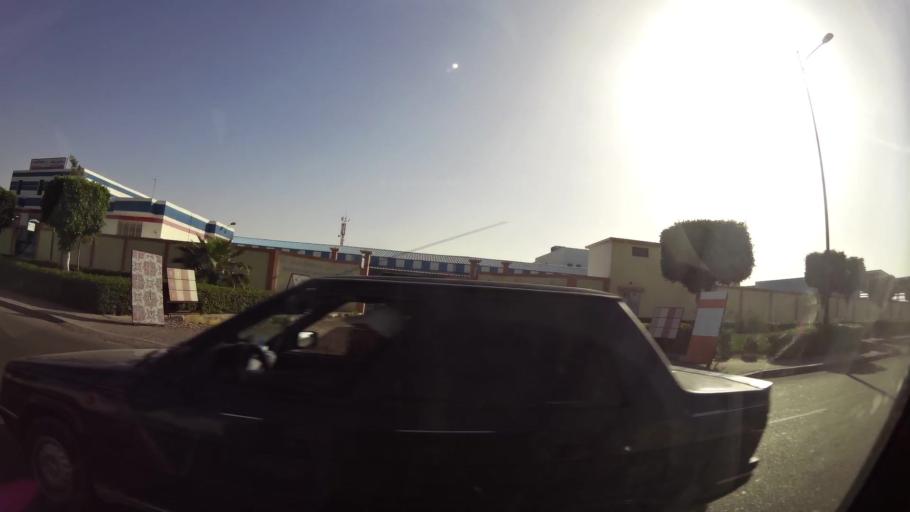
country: MA
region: Oued ed Dahab-Lagouira
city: Dakhla
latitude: 30.3894
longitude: -9.5278
